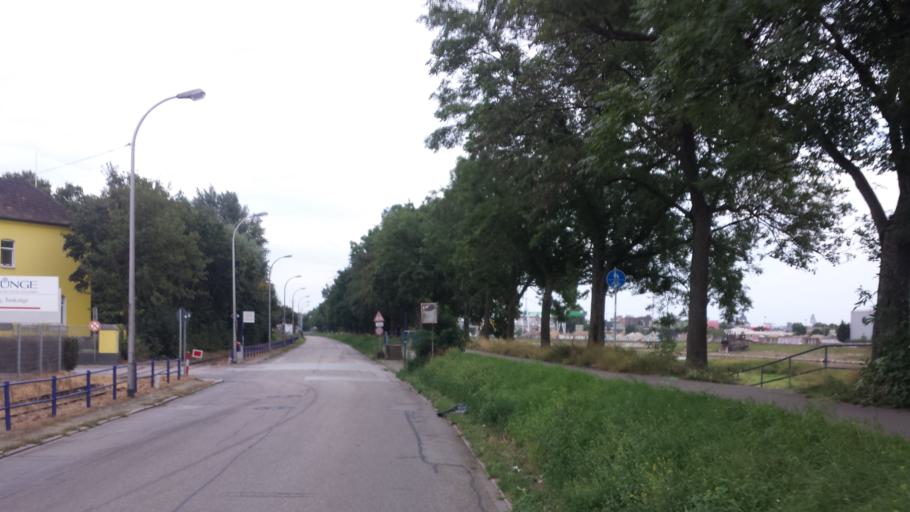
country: DE
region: Rheinland-Pfalz
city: Ludwigshafen am Rhein
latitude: 49.5052
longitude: 8.4493
